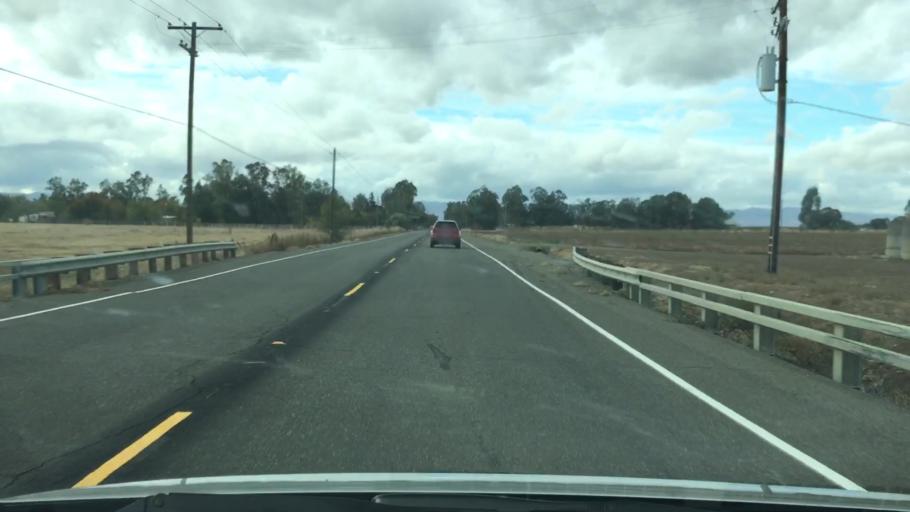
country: US
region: California
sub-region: Yolo County
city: Davis
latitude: 38.5616
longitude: -121.8464
